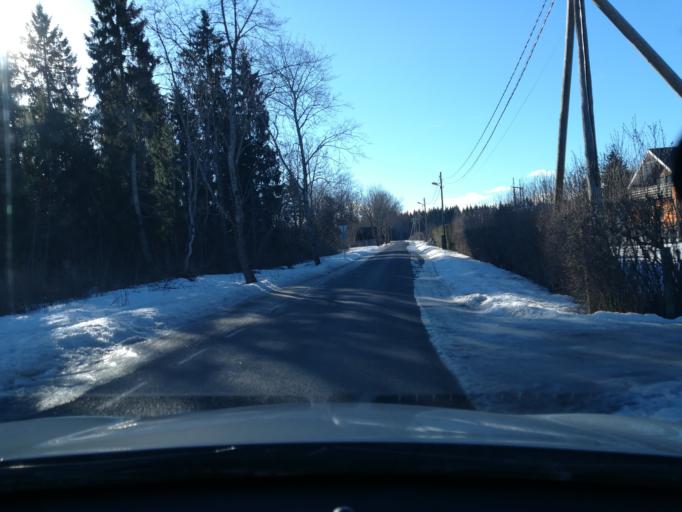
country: EE
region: Raplamaa
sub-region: Kohila vald
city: Kohila
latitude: 59.2323
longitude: 24.7640
